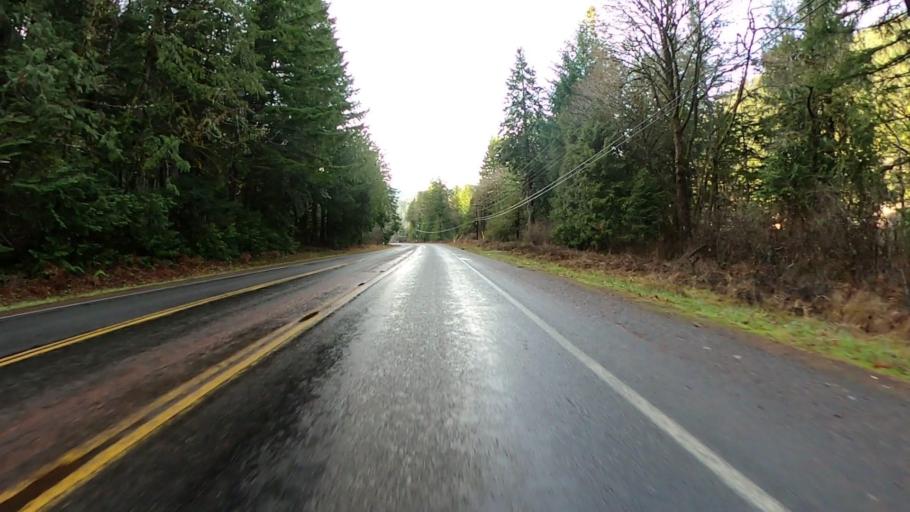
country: US
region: Oregon
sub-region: Lane County
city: Oakridge
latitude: 43.7571
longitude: -122.5128
